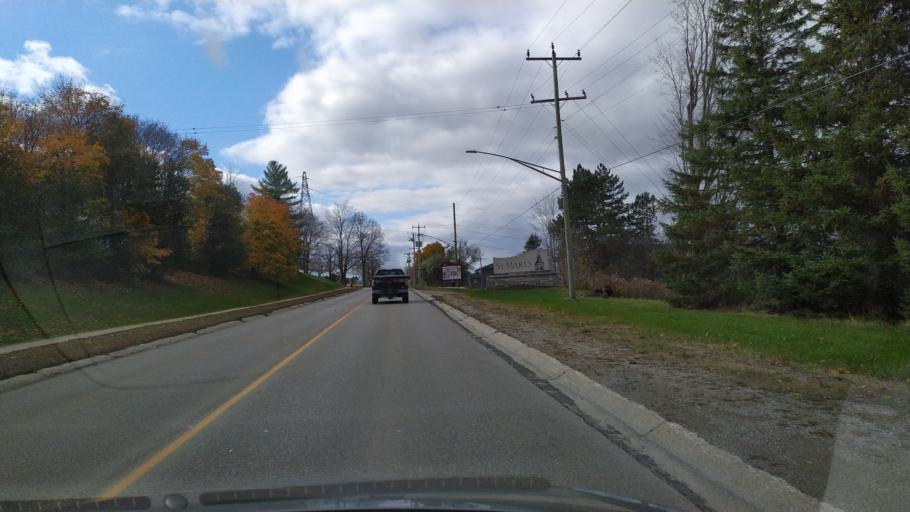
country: CA
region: Ontario
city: Stratford
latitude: 43.2617
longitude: -81.1214
